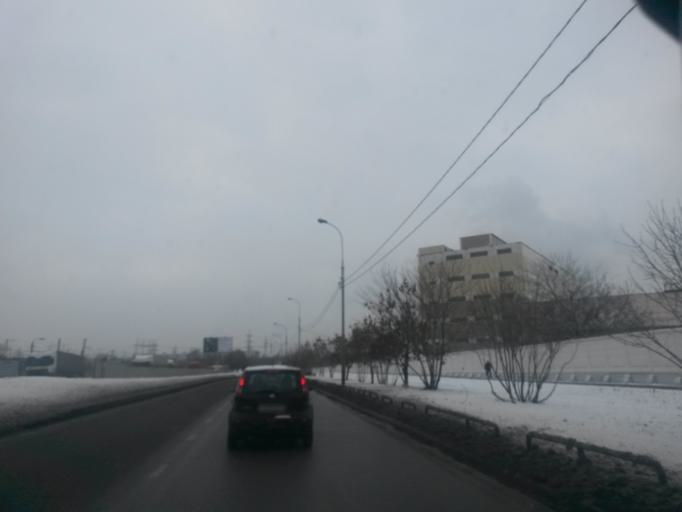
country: RU
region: Moscow
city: Mikhalkovo
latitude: 55.6731
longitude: 37.4346
